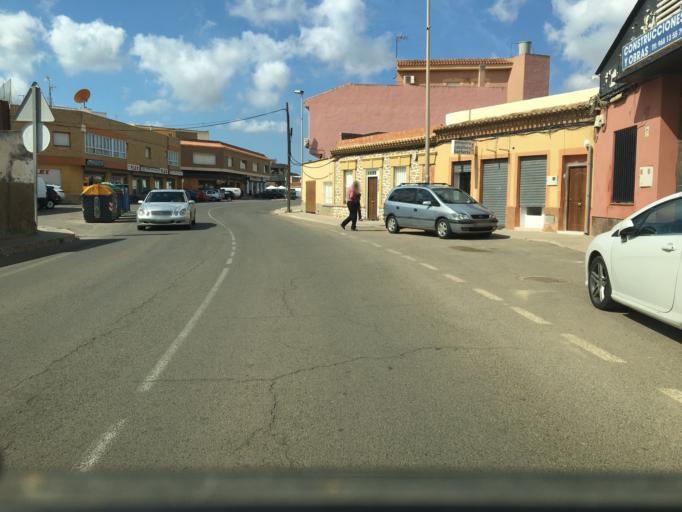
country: ES
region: Murcia
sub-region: Murcia
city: La Union
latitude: 37.6469
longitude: -0.8697
